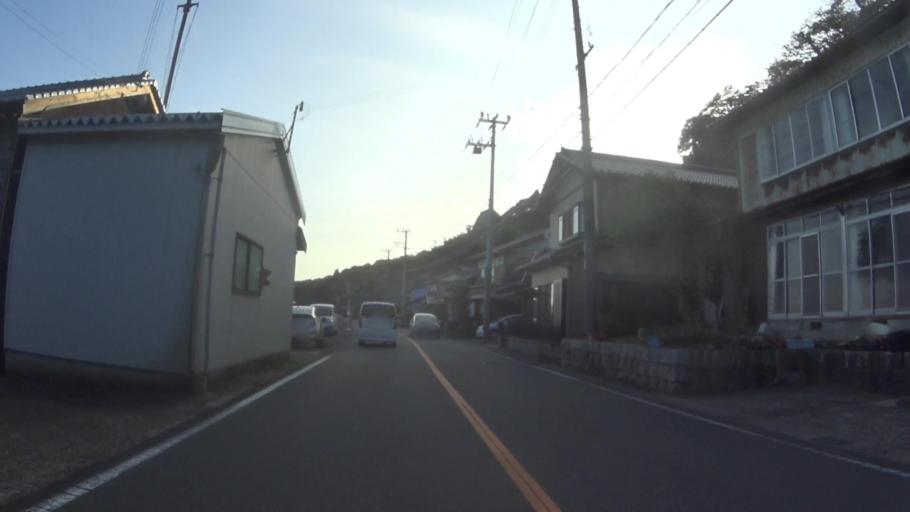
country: JP
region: Kyoto
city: Miyazu
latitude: 35.6482
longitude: 135.2537
